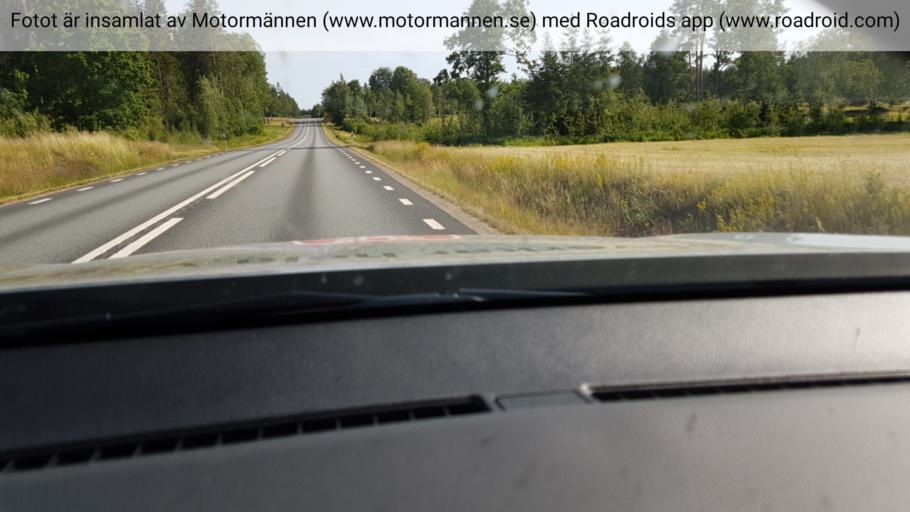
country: SE
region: Joenkoeping
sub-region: Vetlanda Kommun
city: Ekenassjon
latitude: 57.5245
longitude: 14.9890
